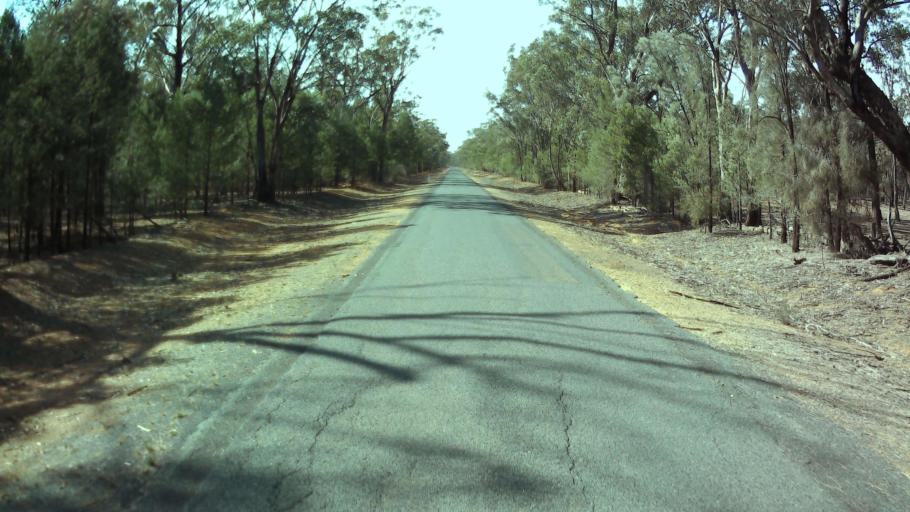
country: AU
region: New South Wales
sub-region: Weddin
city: Grenfell
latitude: -33.7151
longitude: 148.0249
